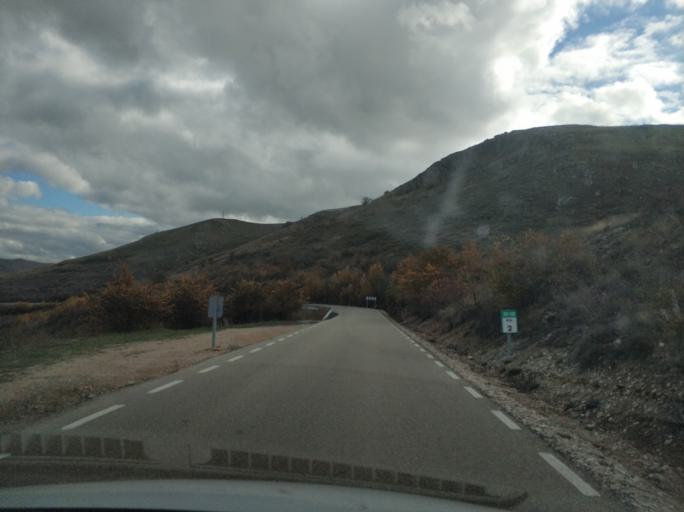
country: ES
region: Castille and Leon
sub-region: Provincia de Soria
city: Medinaceli
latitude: 41.1646
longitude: -2.4327
